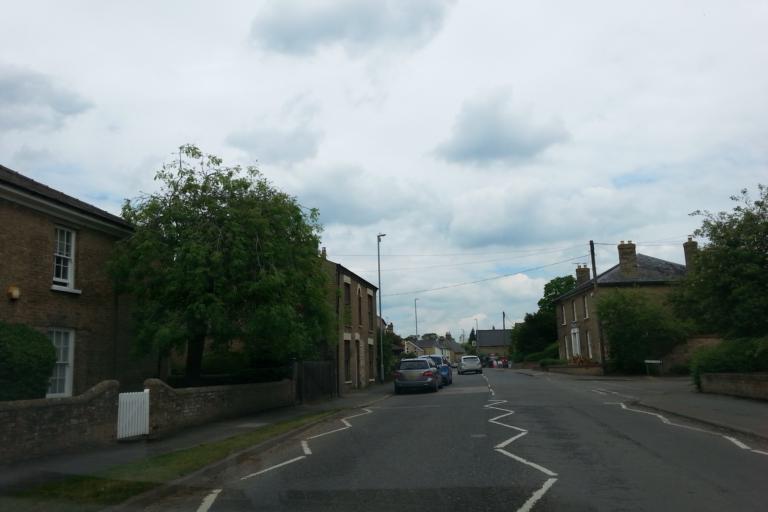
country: GB
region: England
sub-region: Cambridgeshire
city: Earith
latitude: 52.3120
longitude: 0.0560
